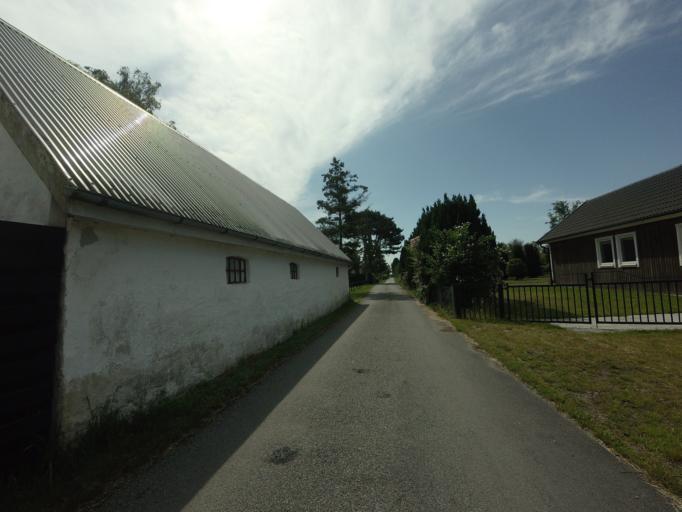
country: SE
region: Skane
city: Smygehamn
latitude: 55.3582
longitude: 13.4199
